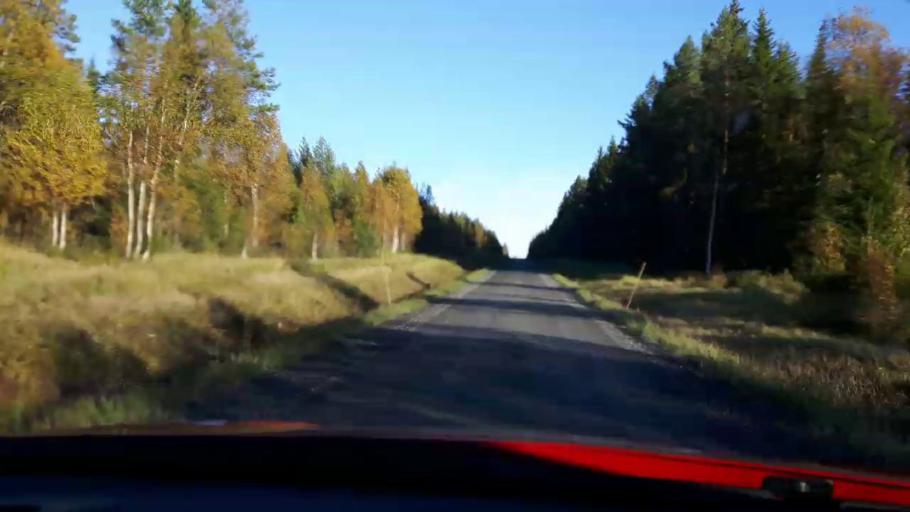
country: SE
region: Jaemtland
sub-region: OEstersunds Kommun
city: Lit
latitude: 63.5997
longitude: 14.8145
